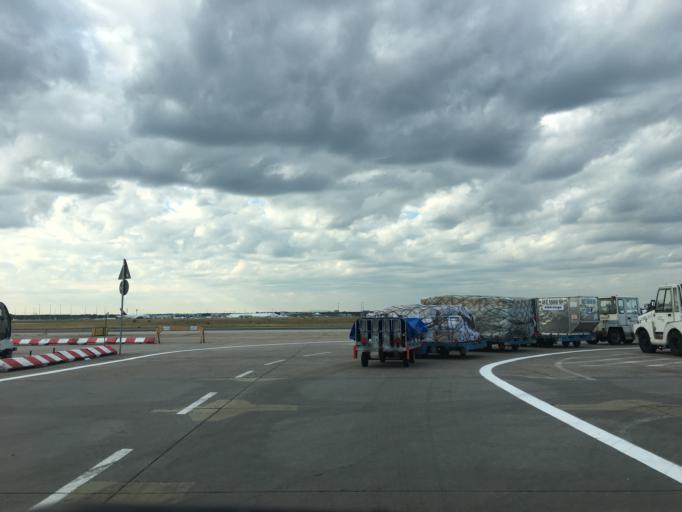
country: DE
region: Hesse
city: Kelsterbach
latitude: 50.0427
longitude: 8.5650
